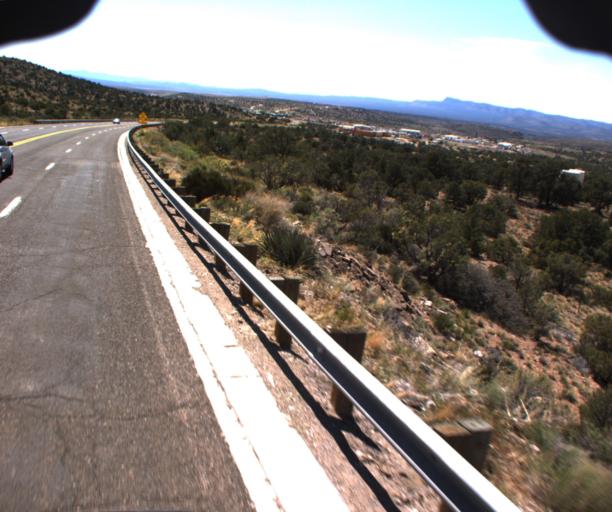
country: US
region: Arizona
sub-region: Mohave County
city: Peach Springs
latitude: 35.5438
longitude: -113.4028
